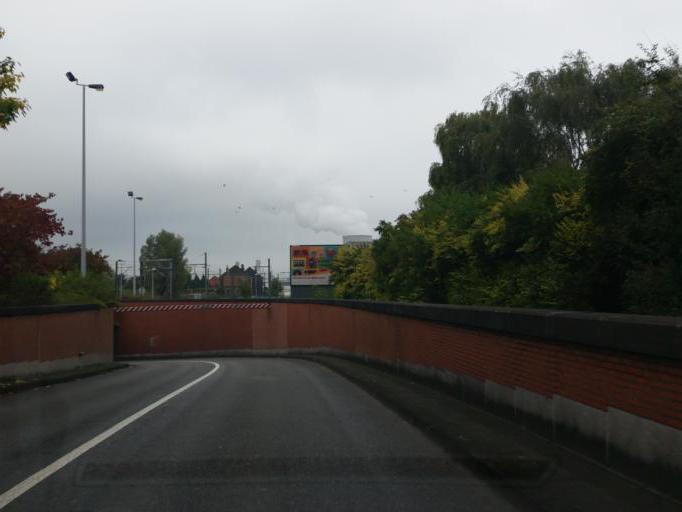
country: BE
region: Flanders
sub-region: Provincie Vlaams-Brabant
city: Drogenbos
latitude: 50.7913
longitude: 4.2961
